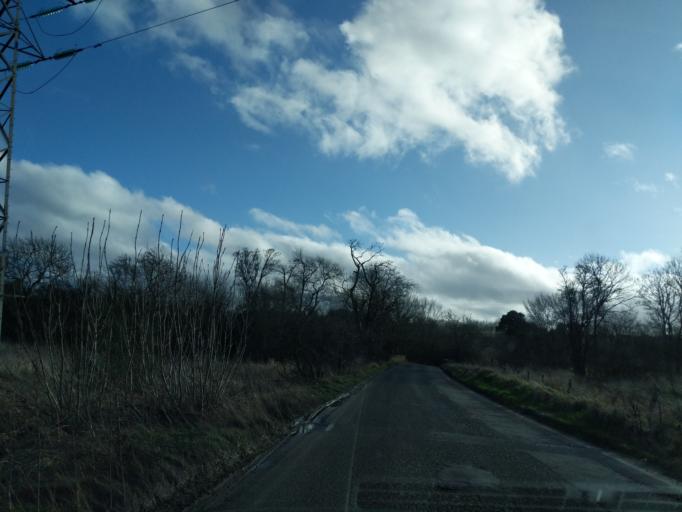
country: GB
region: Scotland
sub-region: Edinburgh
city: Balerno
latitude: 55.8969
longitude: -3.3498
